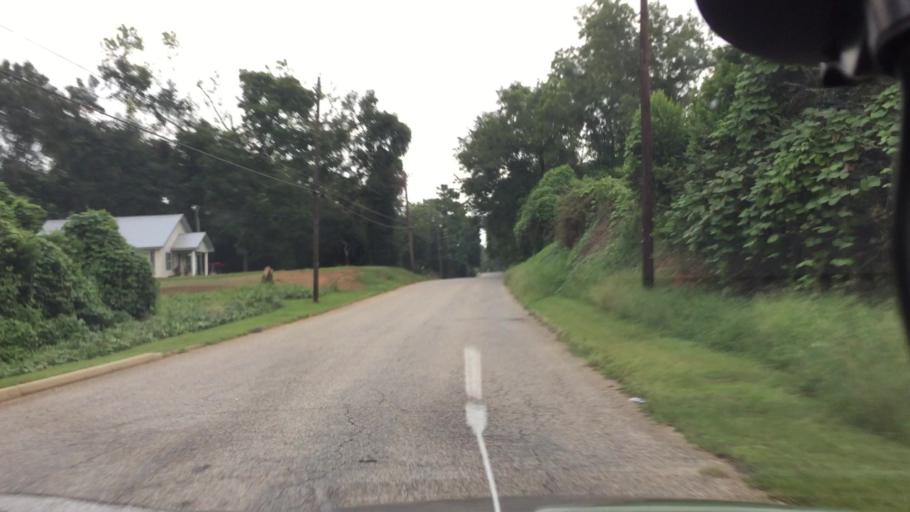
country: US
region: Alabama
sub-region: Coffee County
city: Enterprise
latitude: 31.3131
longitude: -85.8458
